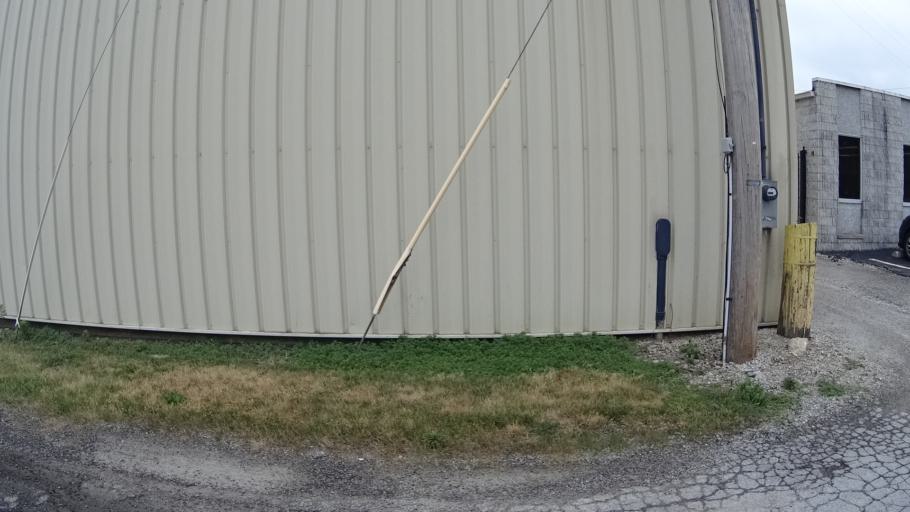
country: US
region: Ohio
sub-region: Erie County
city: Sandusky
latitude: 41.4591
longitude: -82.7058
